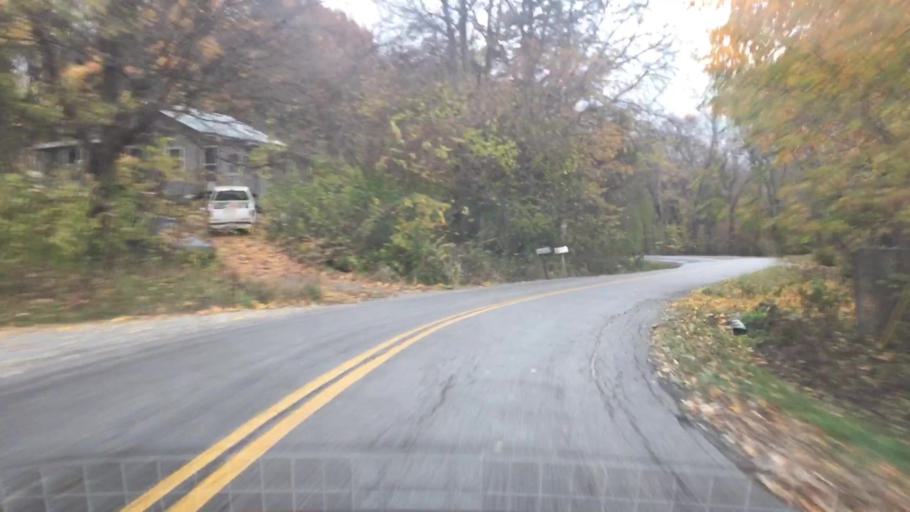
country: US
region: Missouri
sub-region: Boone County
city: Columbia
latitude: 38.9121
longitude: -92.4718
